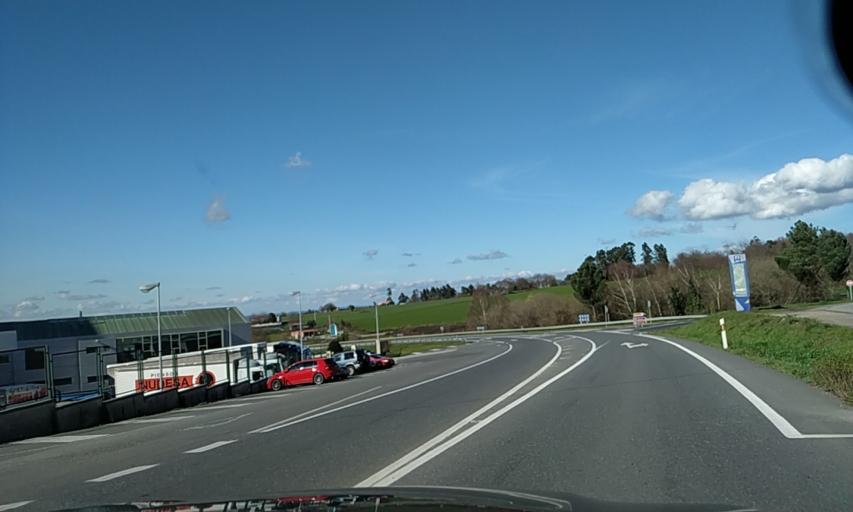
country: ES
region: Galicia
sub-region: Provincia de Pontevedra
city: Silleda
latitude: 42.7044
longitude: -8.2587
